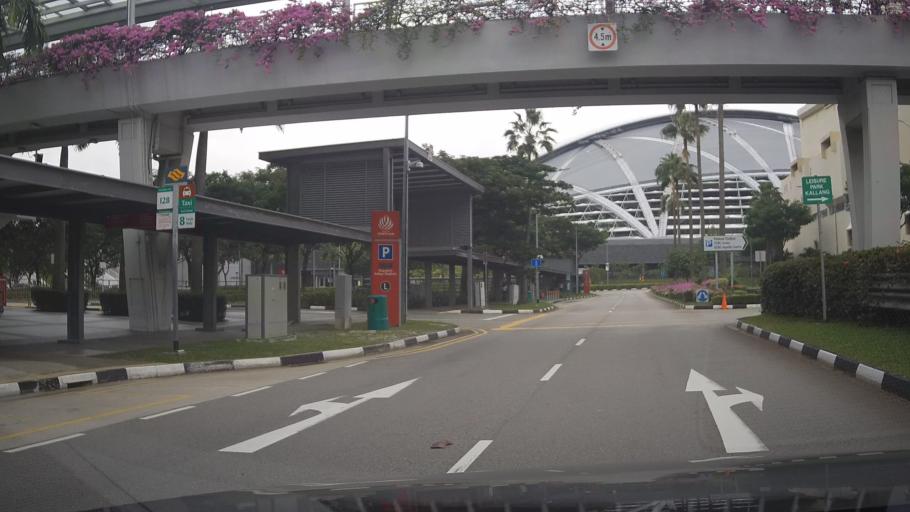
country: SG
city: Singapore
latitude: 1.3010
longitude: 103.8756
